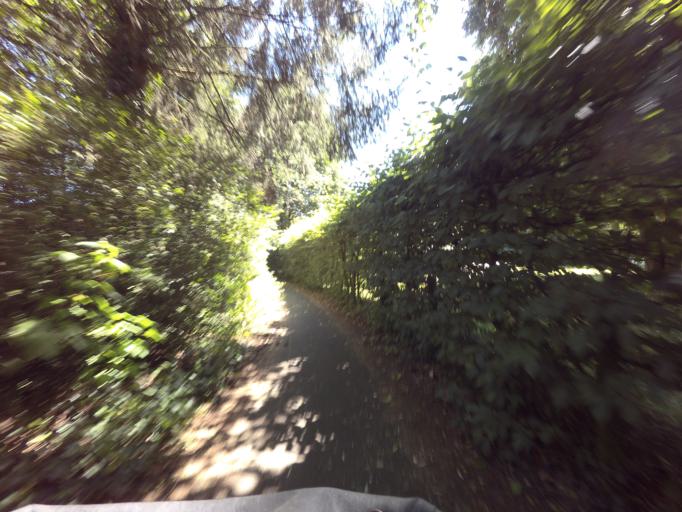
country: NL
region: Utrecht
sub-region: Gemeente De Bilt
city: De Bilt
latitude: 52.1354
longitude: 5.2104
